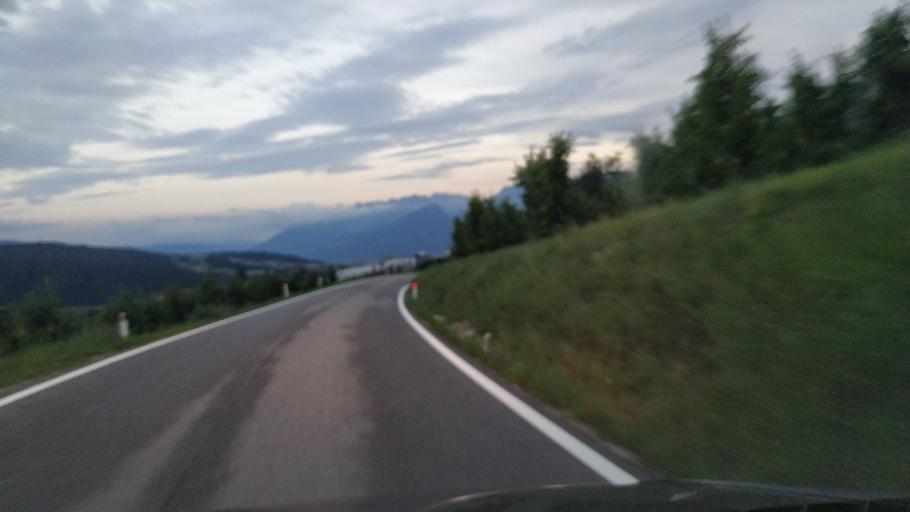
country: IT
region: Trentino-Alto Adige
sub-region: Provincia di Trento
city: Brez
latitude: 46.4384
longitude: 11.1113
